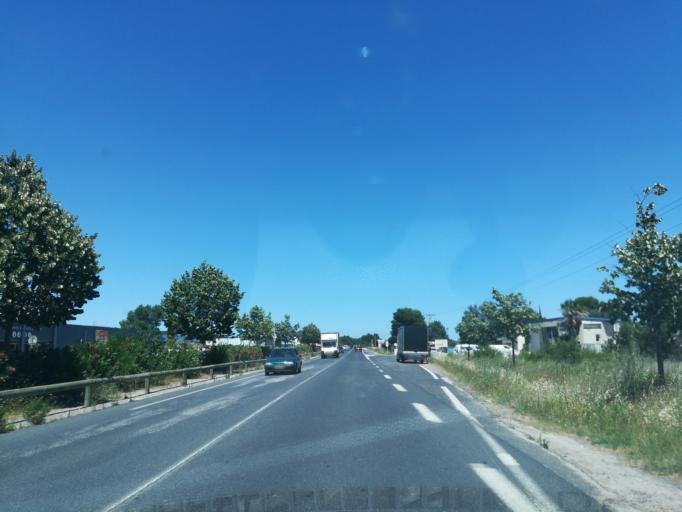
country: FR
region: Languedoc-Roussillon
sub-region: Departement des Pyrenees-Orientales
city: el Volo
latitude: 42.5342
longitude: 2.8417
